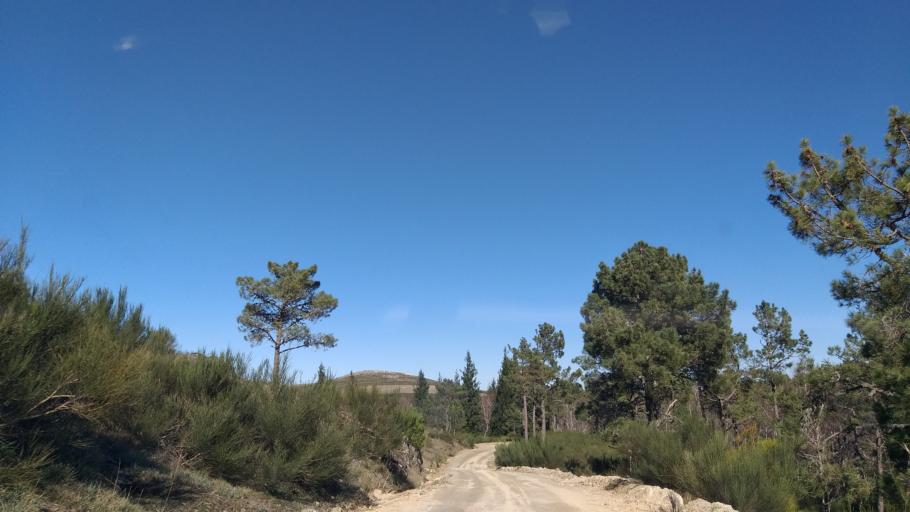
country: PT
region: Guarda
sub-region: Manteigas
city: Manteigas
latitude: 40.4973
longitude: -7.4906
